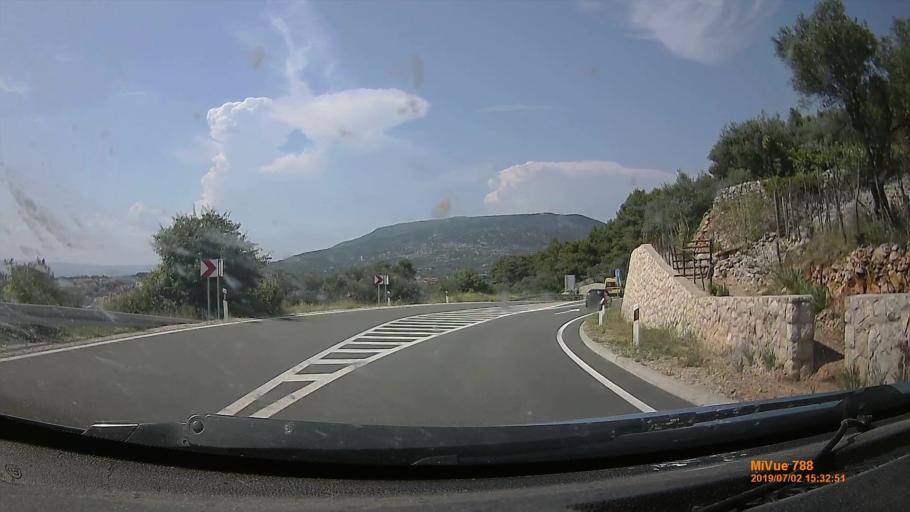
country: HR
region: Primorsko-Goranska
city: Cres
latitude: 44.9551
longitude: 14.4179
